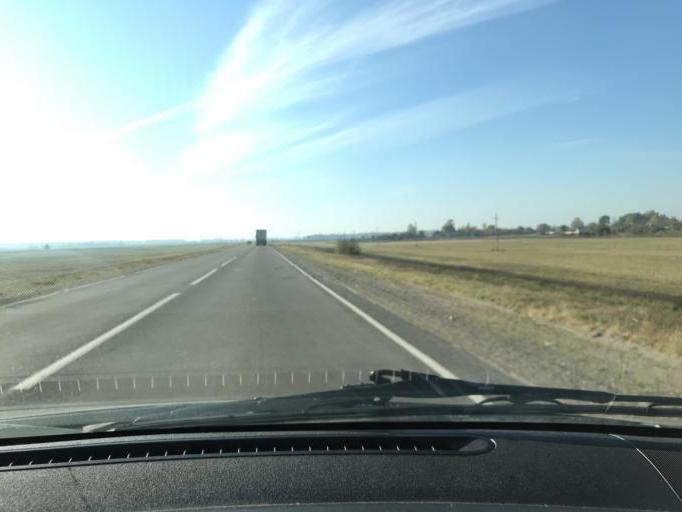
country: BY
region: Brest
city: Asnyezhytsy
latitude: 52.2851
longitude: 26.4094
